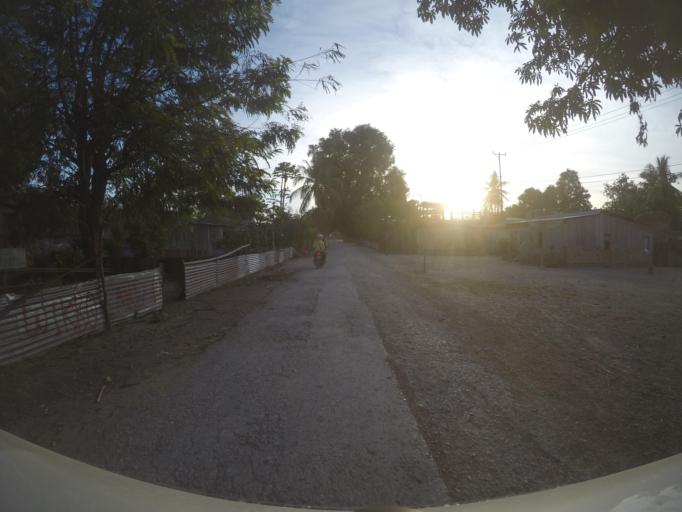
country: TL
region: Viqueque
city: Viqueque
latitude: -8.9435
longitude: 126.4498
